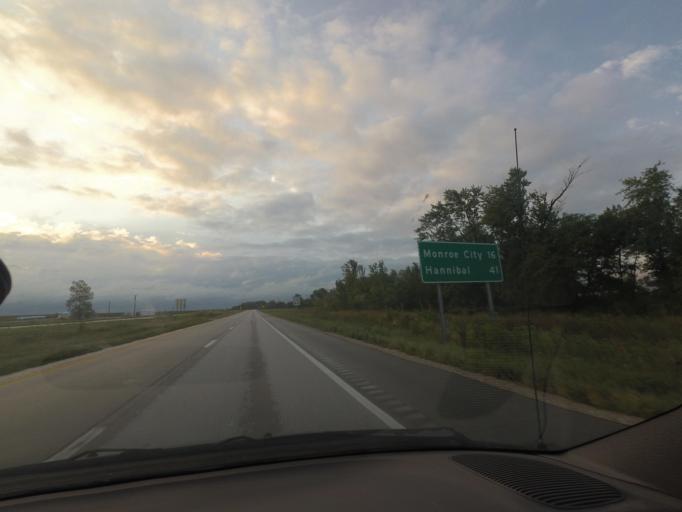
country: US
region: Missouri
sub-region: Shelby County
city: Shelbina
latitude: 39.6927
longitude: -92.0245
